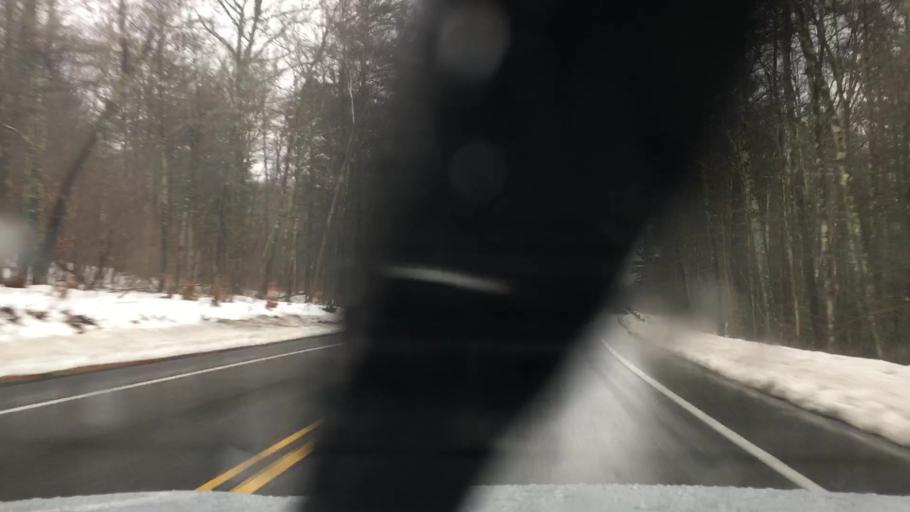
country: US
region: Massachusetts
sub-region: Franklin County
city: Shutesbury
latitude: 42.4770
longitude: -72.3495
